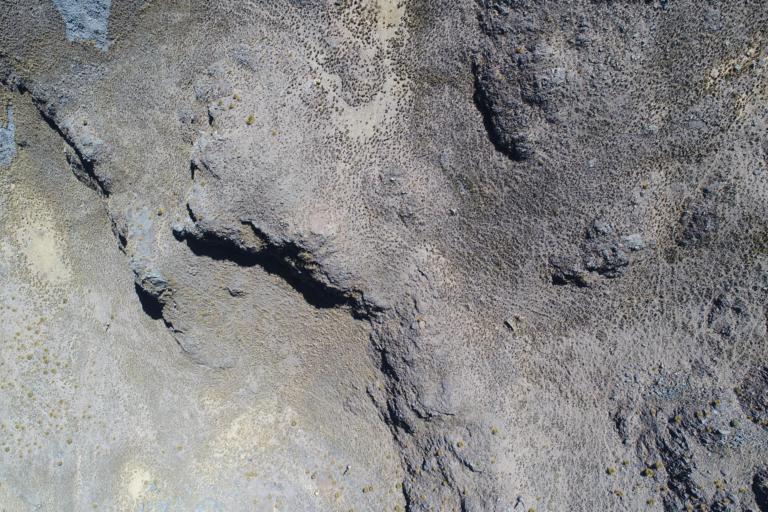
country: BO
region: La Paz
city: Viloco
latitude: -16.8083
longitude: -67.5446
